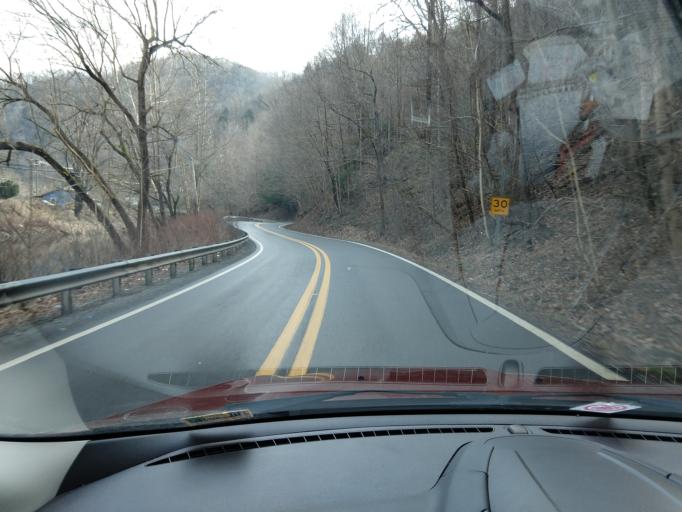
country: US
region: West Virginia
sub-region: McDowell County
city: Welch
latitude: 37.3378
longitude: -81.7315
